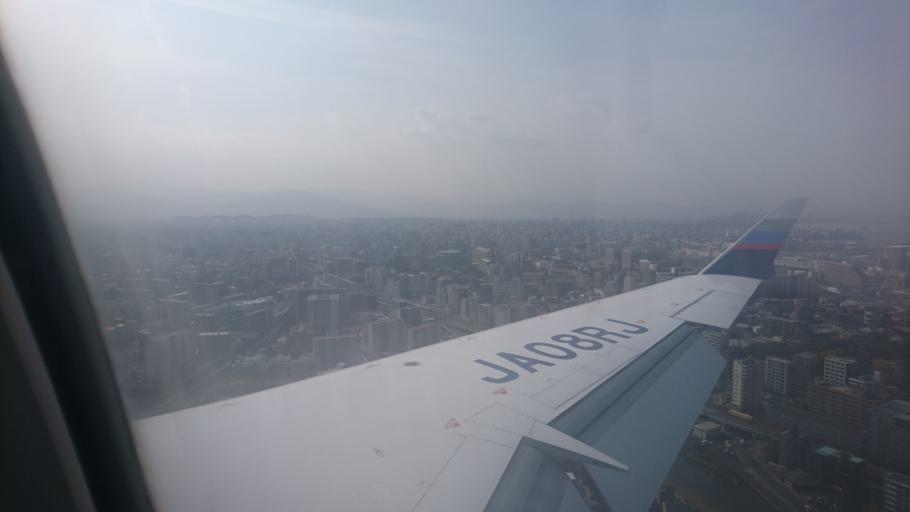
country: JP
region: Fukuoka
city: Fukuoka-shi
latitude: 33.6155
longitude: 130.4302
